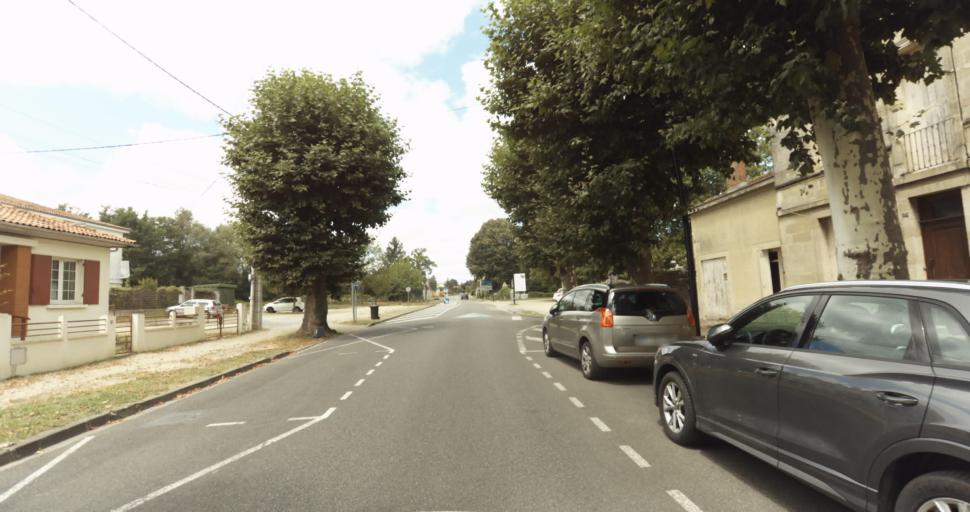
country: FR
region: Aquitaine
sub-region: Departement de la Gironde
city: Bazas
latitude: 44.4344
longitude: -0.2167
